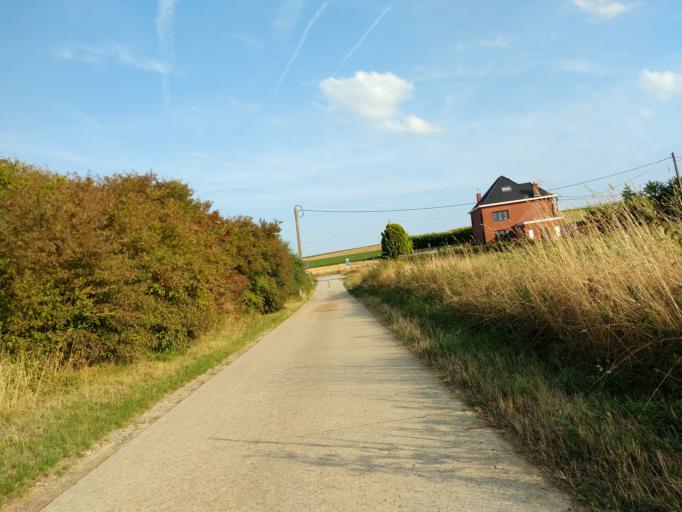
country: BE
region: Flanders
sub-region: Provincie Vlaams-Brabant
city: Bierbeek
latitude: 50.8319
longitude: 4.7879
